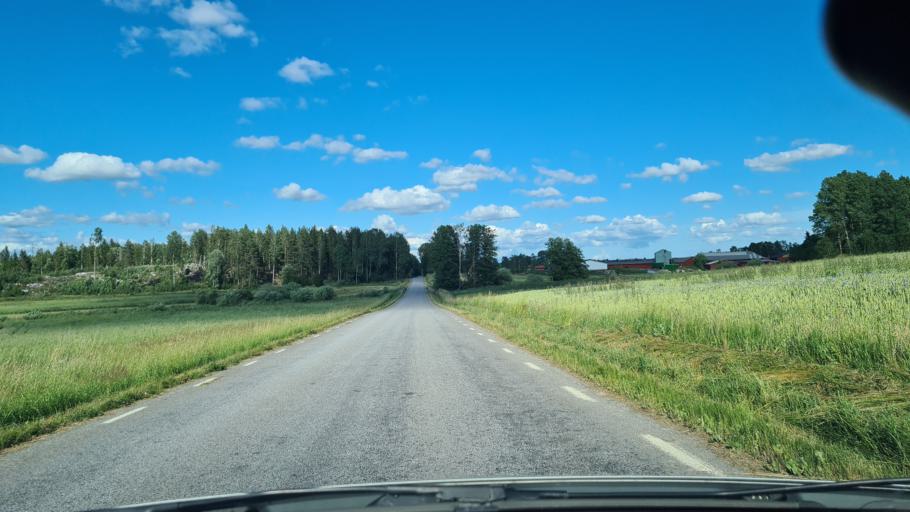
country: SE
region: Soedermanland
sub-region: Nykopings Kommun
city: Olstorp
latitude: 58.8174
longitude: 16.4844
